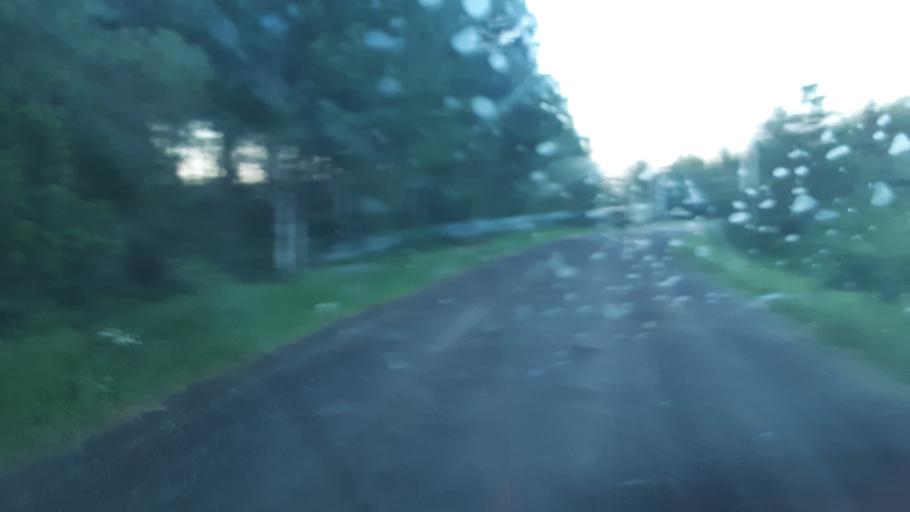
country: US
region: Maine
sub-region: Aroostook County
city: Caribou
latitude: 46.8482
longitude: -68.1358
